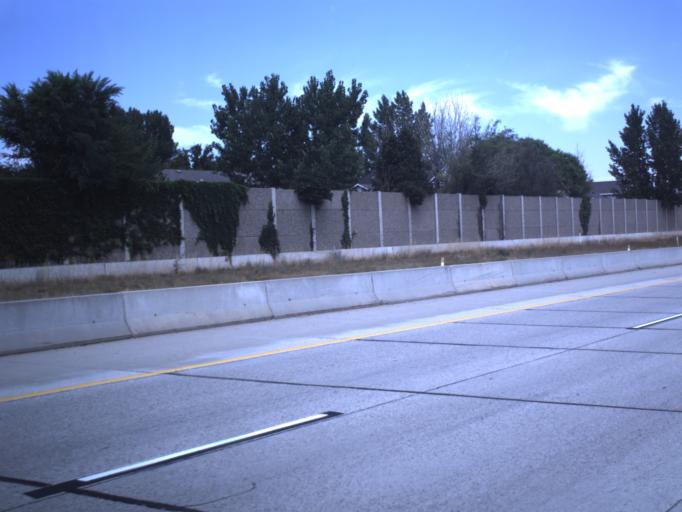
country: US
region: Utah
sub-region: Salt Lake County
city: South Jordan Heights
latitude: 40.5783
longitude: -111.9770
